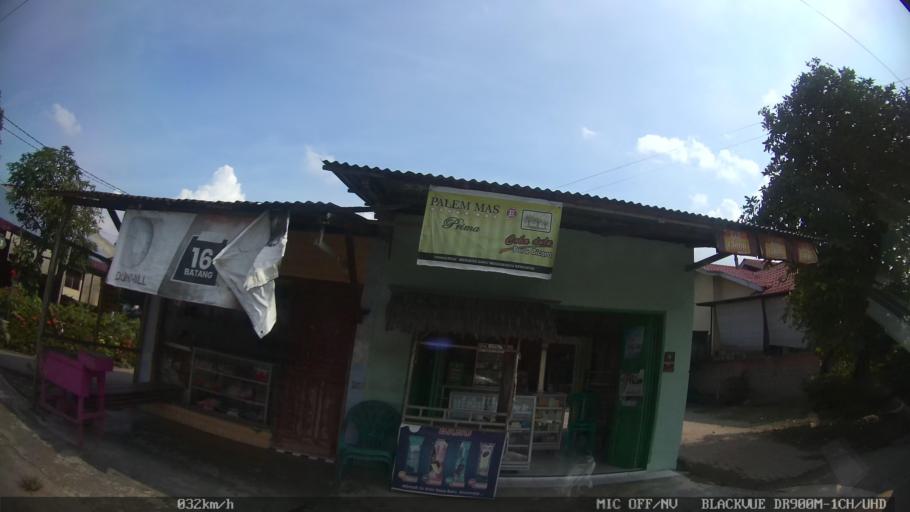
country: ID
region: North Sumatra
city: Binjai
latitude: 3.6438
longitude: 98.5159
